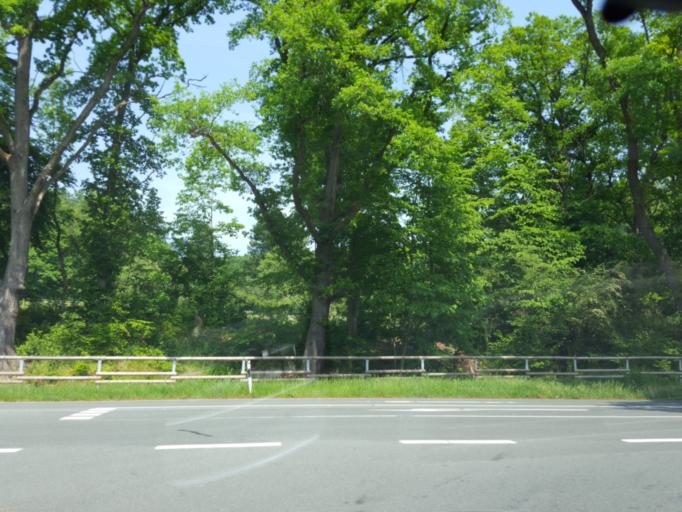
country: DE
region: North Rhine-Westphalia
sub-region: Regierungsbezirk Arnsberg
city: Bestwig
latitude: 51.3476
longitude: 8.4344
